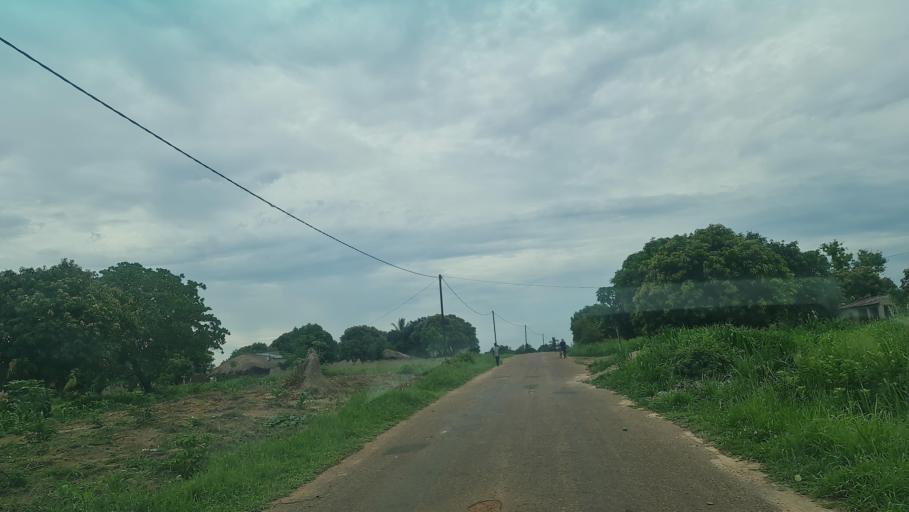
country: MW
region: Southern Region
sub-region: Nsanje District
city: Nsanje
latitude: -17.6748
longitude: 35.7193
